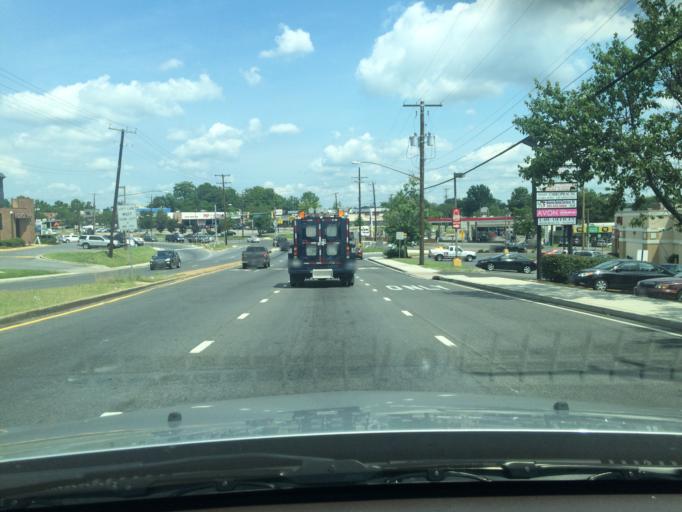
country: US
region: Maryland
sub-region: Prince George's County
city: Langley Park
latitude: 38.9827
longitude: -76.9791
